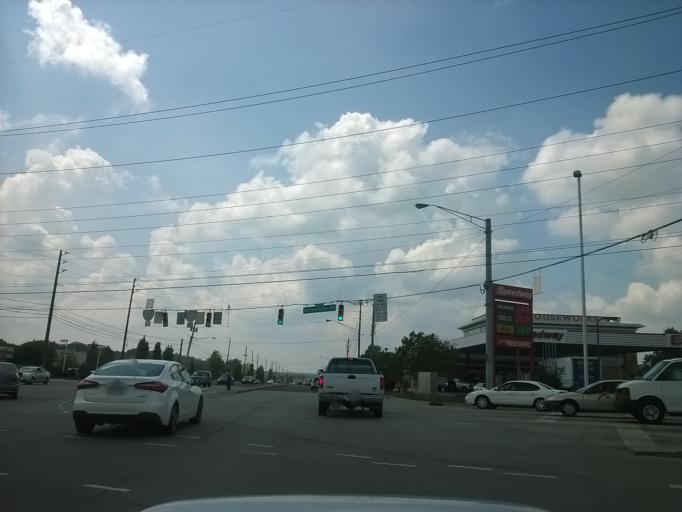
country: US
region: Indiana
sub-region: Marion County
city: Broad Ripple
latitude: 39.9052
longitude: -86.0784
